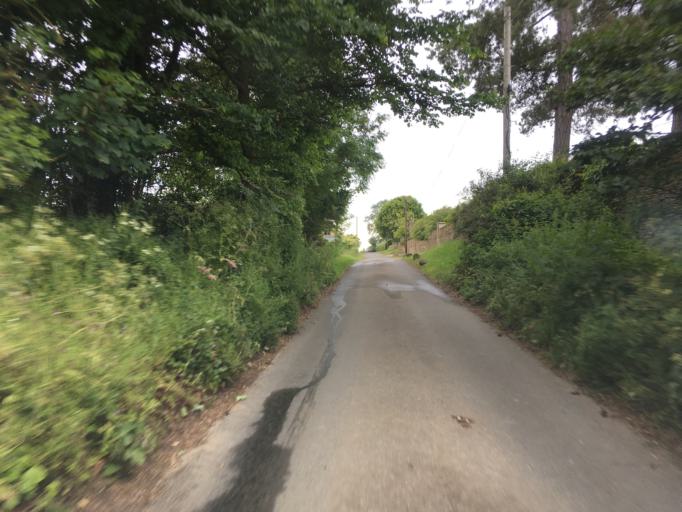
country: GB
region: England
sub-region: Wiltshire
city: Norton
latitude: 51.5835
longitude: -2.1991
